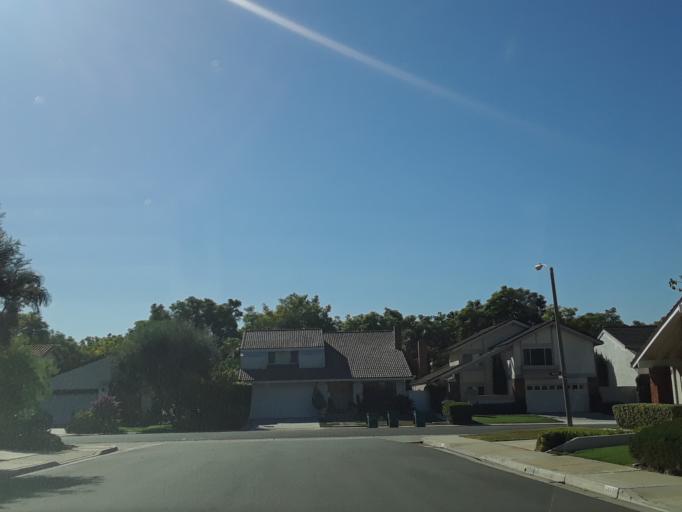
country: US
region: California
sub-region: Orange County
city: Tustin
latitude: 33.7104
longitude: -117.7928
